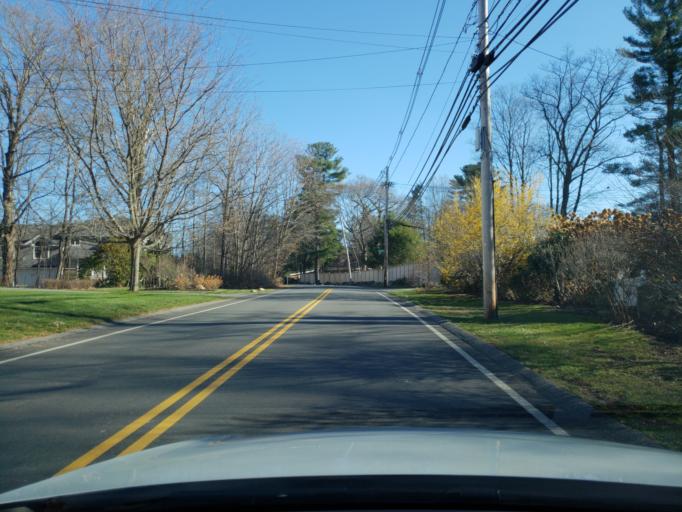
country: US
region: Massachusetts
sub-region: Essex County
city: Andover
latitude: 42.6392
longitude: -71.1351
